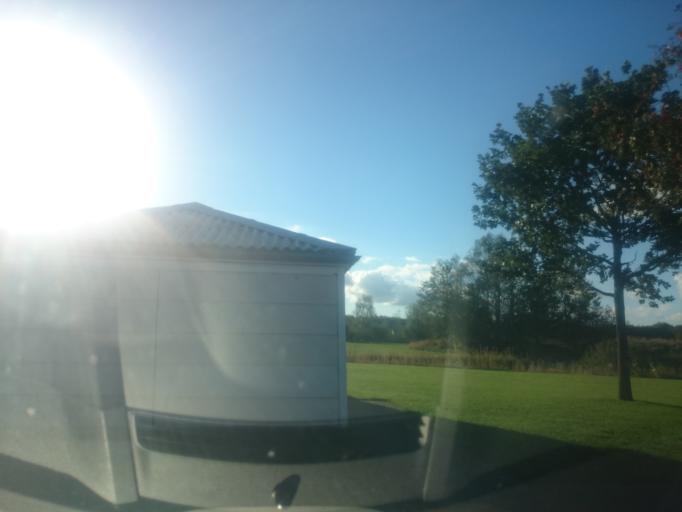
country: DK
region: South Denmark
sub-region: Billund Kommune
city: Billund
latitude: 55.7208
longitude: 9.1187
